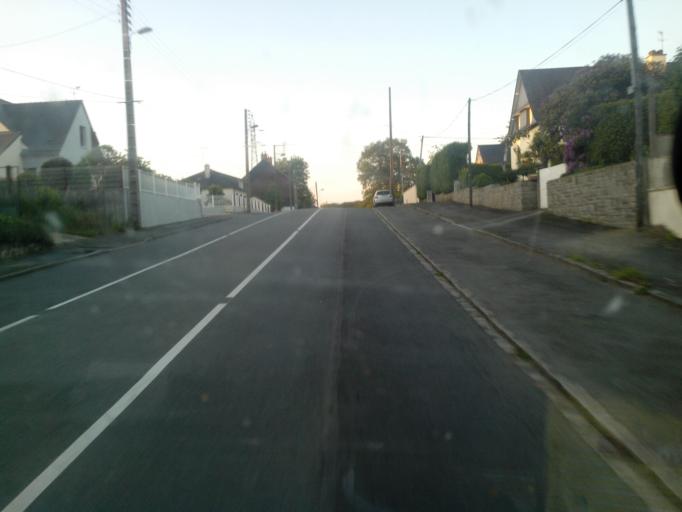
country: FR
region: Brittany
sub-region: Departement d'Ille-et-Vilaine
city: Fougeres
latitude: 48.3681
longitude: -1.1832
